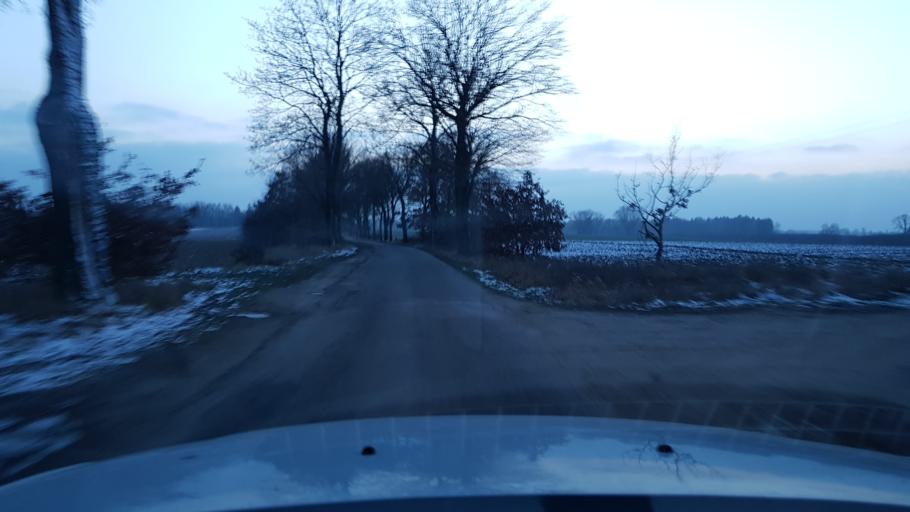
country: PL
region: West Pomeranian Voivodeship
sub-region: Powiat swidwinski
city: Slawoborze
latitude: 53.9567
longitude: 15.7451
